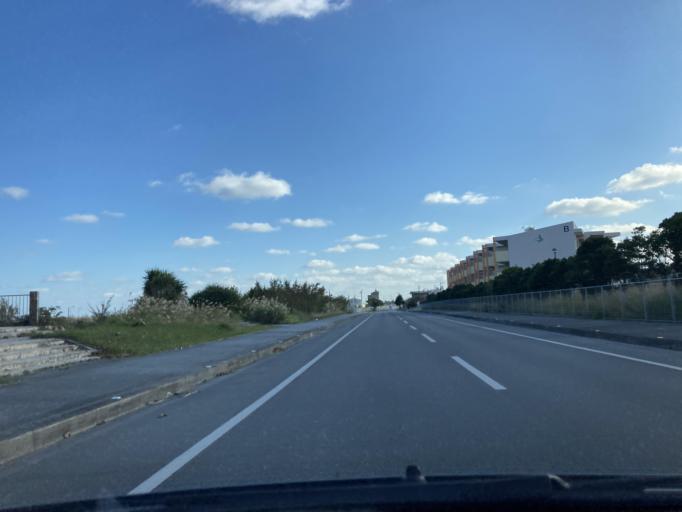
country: JP
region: Okinawa
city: Katsuren-haebaru
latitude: 26.3122
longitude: 127.9194
